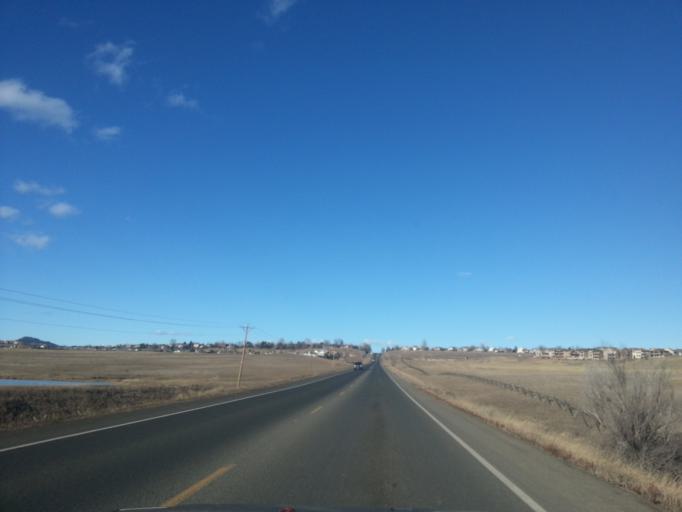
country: US
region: Colorado
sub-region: Larimer County
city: Fort Collins
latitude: 40.5171
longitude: -105.1151
